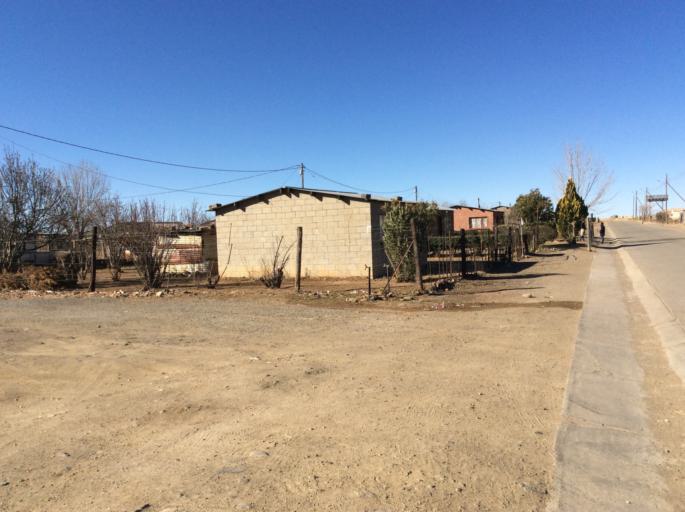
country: ZA
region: Orange Free State
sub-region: Lejweleputswa District Municipality
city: Brandfort
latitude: -28.7339
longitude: 26.1112
